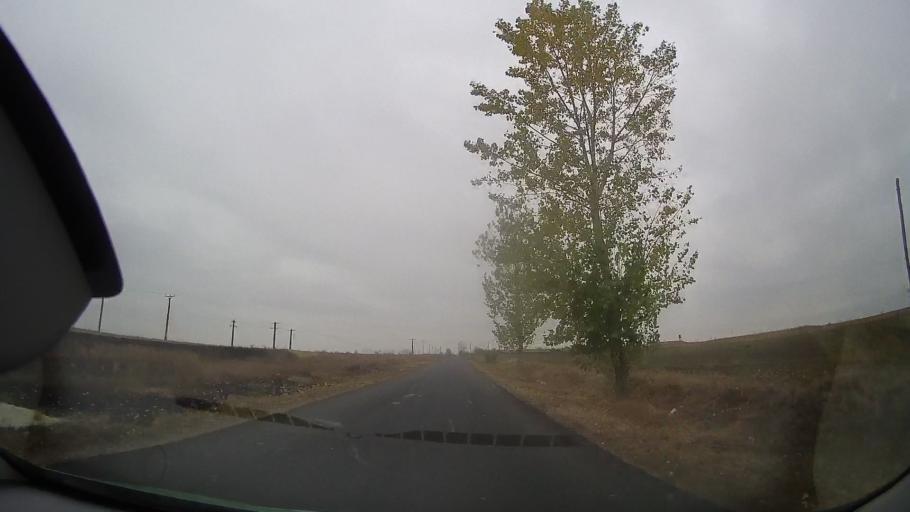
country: RO
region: Braila
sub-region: Comuna Ciocile
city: Ciocile
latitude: 44.8137
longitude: 27.2638
